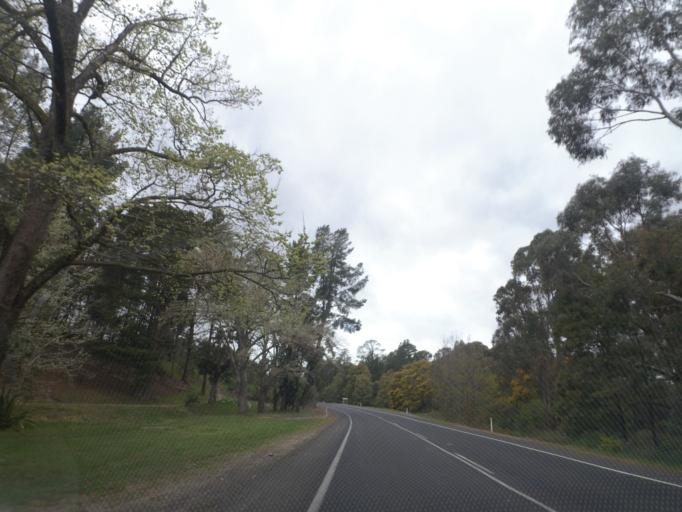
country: AU
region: Victoria
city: Brown Hill
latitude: -37.4186
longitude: 143.9006
